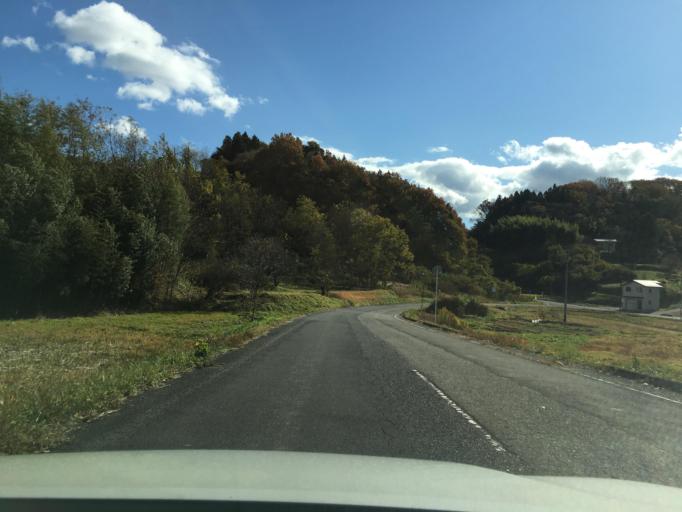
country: JP
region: Fukushima
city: Miharu
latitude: 37.4480
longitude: 140.4569
